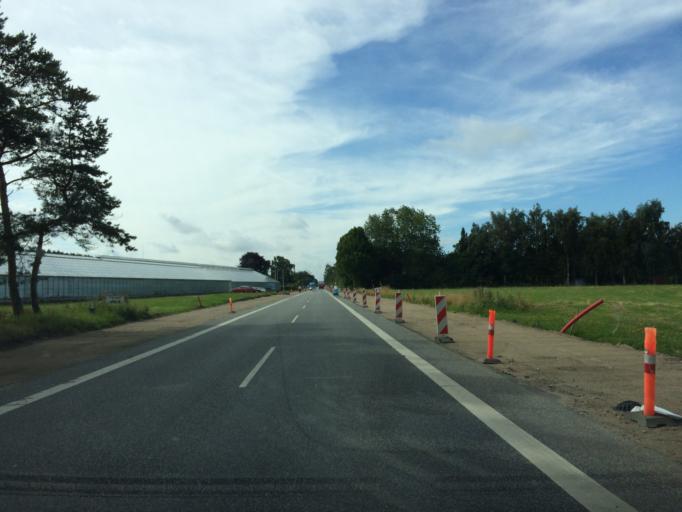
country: DK
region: South Denmark
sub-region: Odense Kommune
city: Bellinge
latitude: 55.3218
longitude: 10.3209
